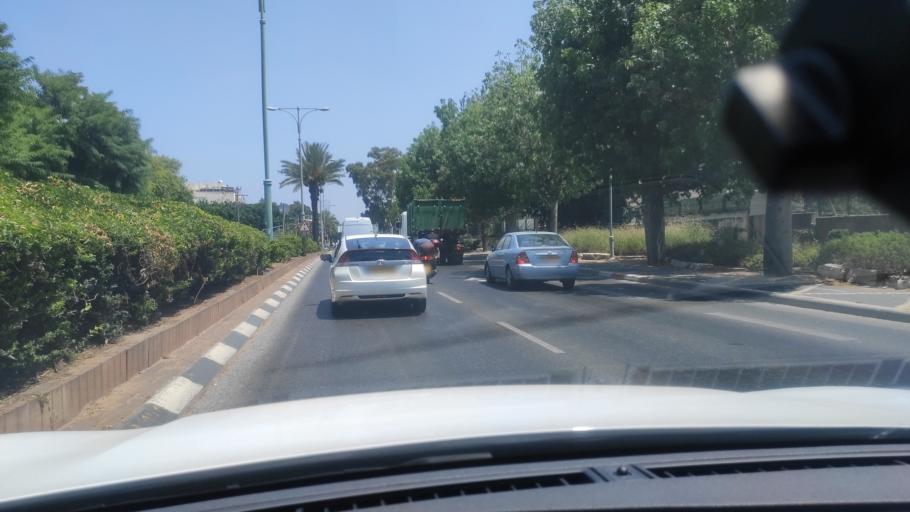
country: IL
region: Central District
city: Petah Tiqwa
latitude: 32.0896
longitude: 34.9018
